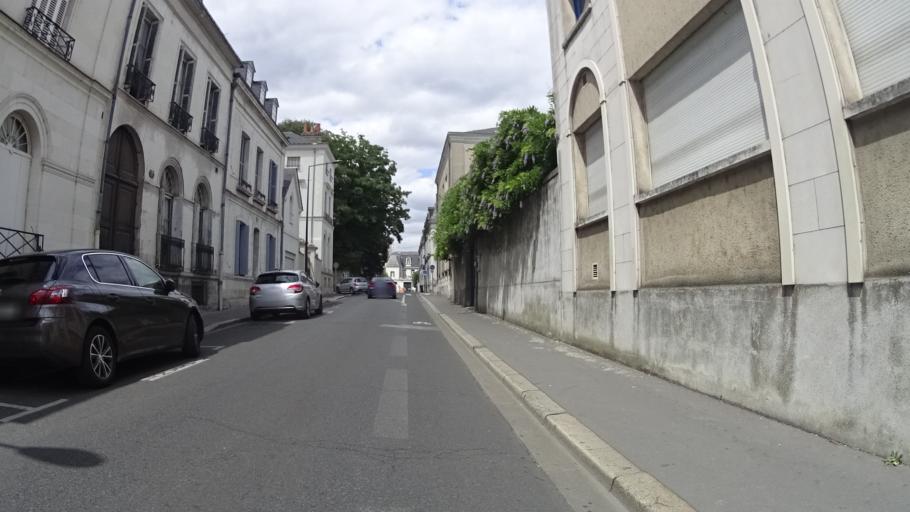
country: FR
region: Centre
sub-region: Departement d'Indre-et-Loire
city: Tours
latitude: 47.3905
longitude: 0.6840
